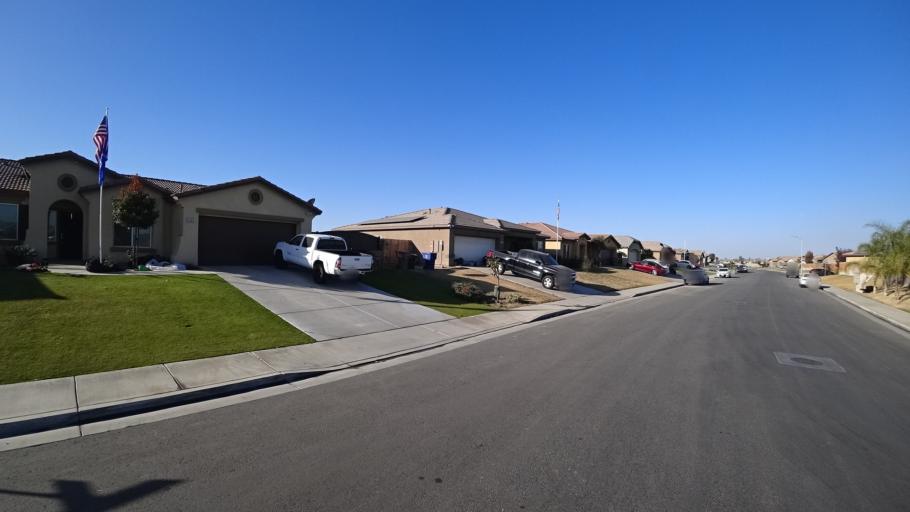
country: US
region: California
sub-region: Kern County
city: Greenfield
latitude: 35.2710
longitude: -119.0279
